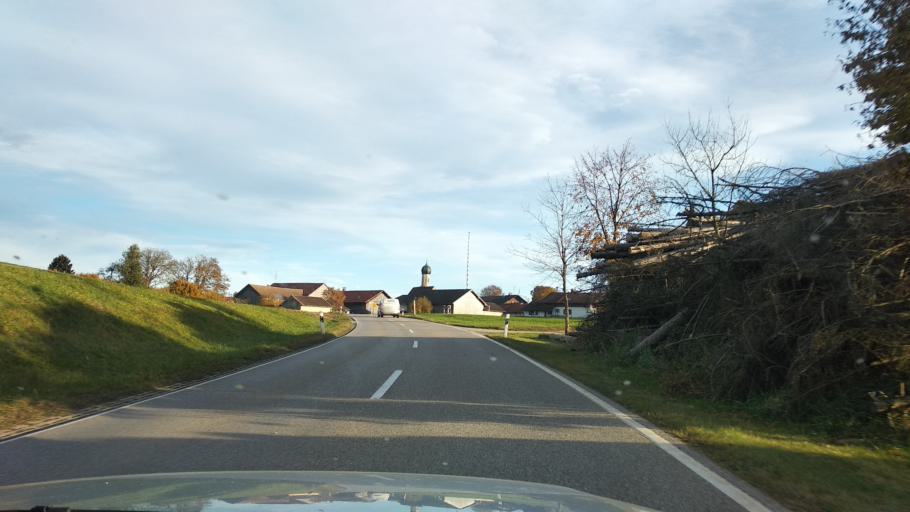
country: DE
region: Bavaria
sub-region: Upper Bavaria
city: Zorneding
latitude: 48.0617
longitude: 11.8483
